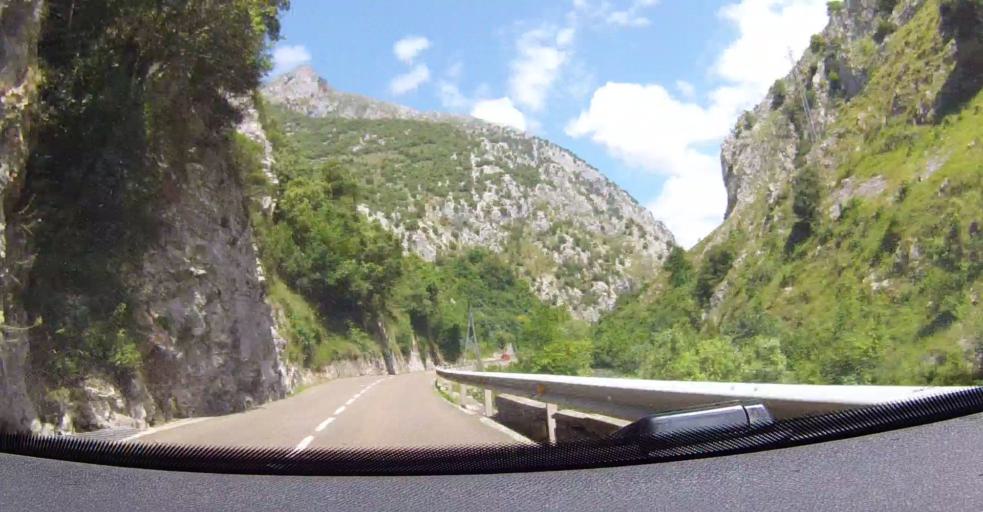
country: ES
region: Cantabria
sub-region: Provincia de Cantabria
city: Tresviso
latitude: 43.2851
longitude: -4.6261
